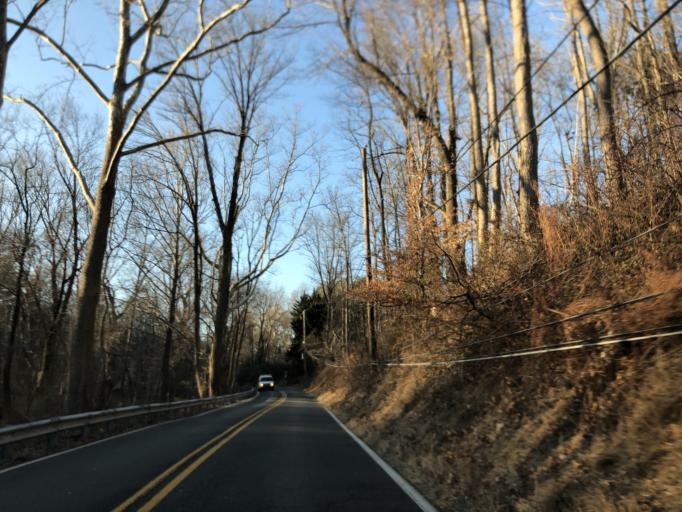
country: US
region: Pennsylvania
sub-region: Delaware County
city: Chester Heights
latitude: 39.8617
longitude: -75.5018
